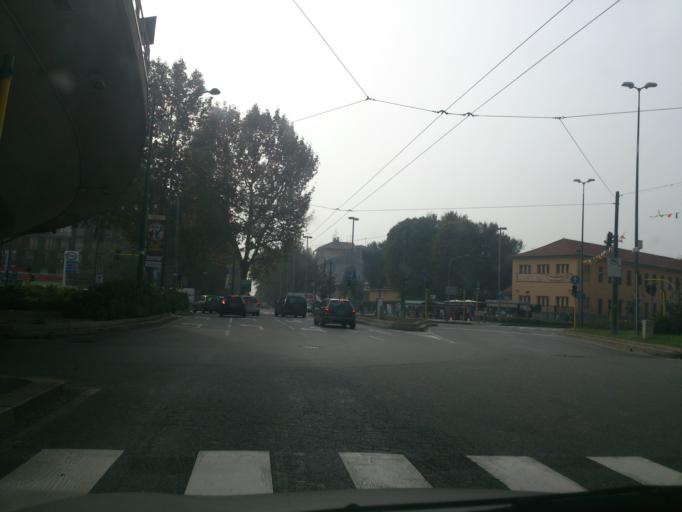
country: IT
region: Lombardy
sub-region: Citta metropolitana di Milano
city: Chiaravalle
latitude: 45.4405
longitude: 9.2241
